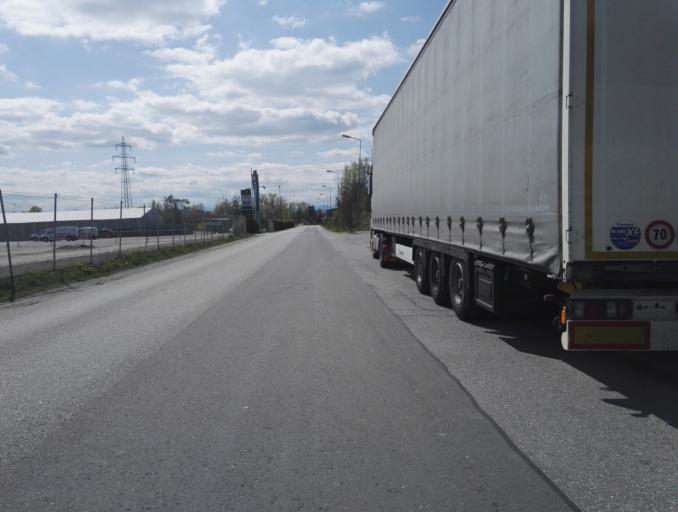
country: AT
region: Styria
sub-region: Politischer Bezirk Graz-Umgebung
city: Raaba
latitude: 47.0402
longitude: 15.4794
